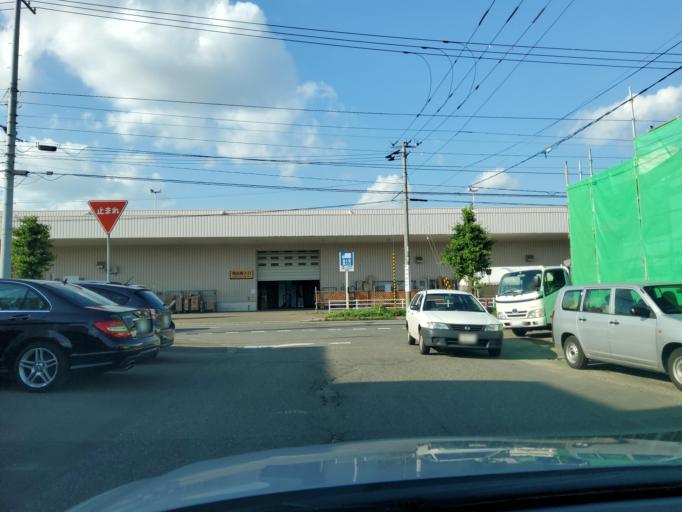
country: JP
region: Hokkaido
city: Obihiro
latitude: 42.8864
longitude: 143.1999
